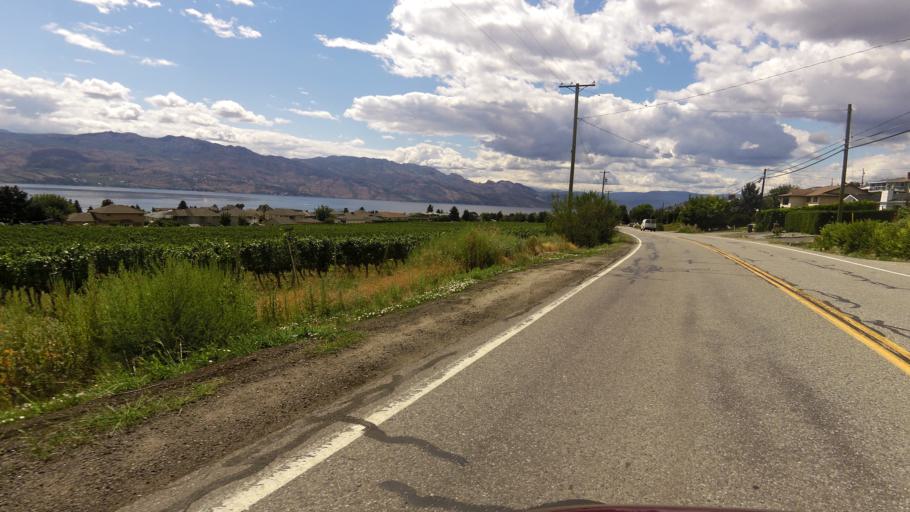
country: CA
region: British Columbia
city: West Kelowna
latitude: 49.8460
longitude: -119.5620
